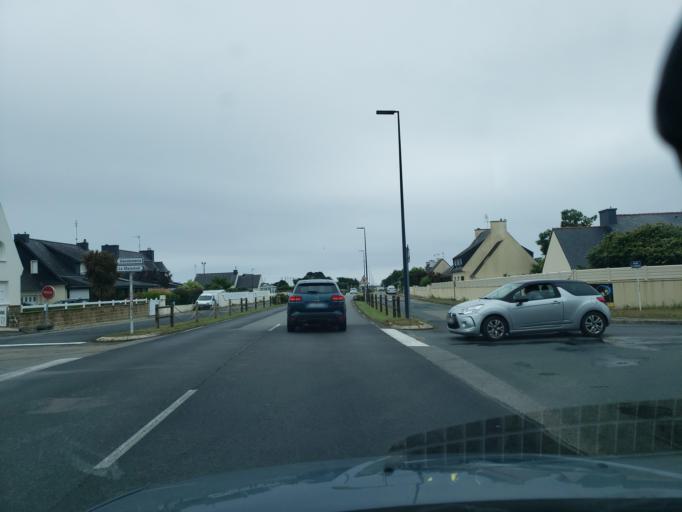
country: FR
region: Brittany
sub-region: Departement du Finistere
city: Guilvinec
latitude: 47.8071
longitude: -4.2799
